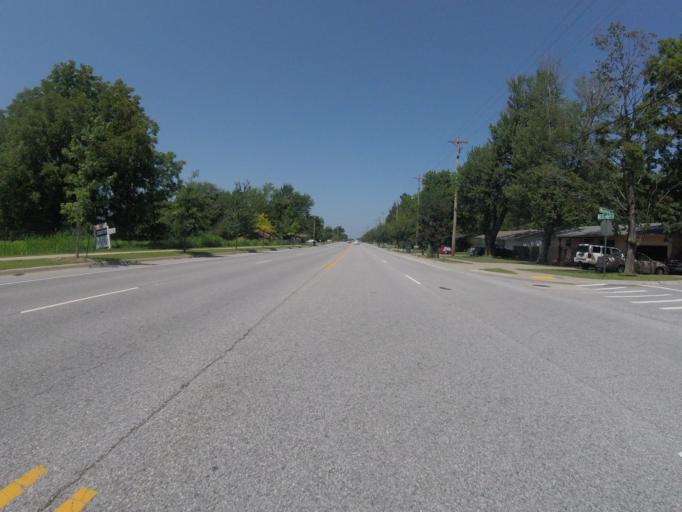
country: US
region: Arkansas
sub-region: Washington County
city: Fayetteville
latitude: 36.0928
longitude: -94.2009
